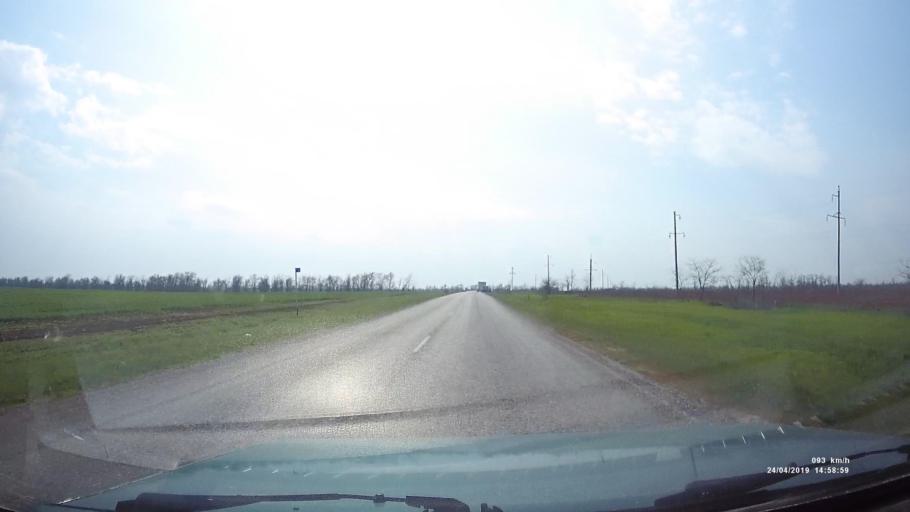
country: RU
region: Rostov
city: Remontnoye
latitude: 46.5678
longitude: 43.5829
